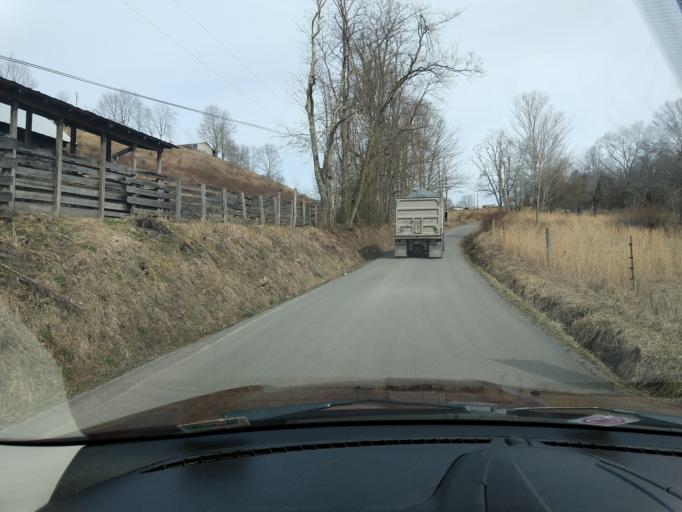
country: US
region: West Virginia
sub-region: Tucker County
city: Parsons
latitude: 39.0110
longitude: -79.5106
